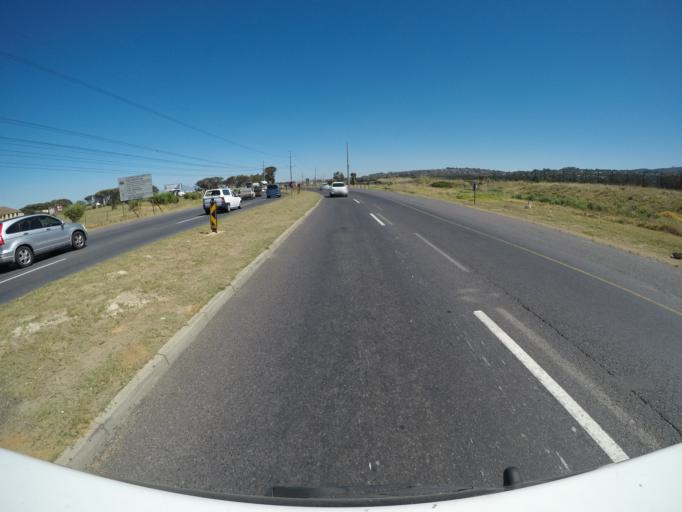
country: ZA
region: Western Cape
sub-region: Cape Winelands District Municipality
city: Stellenbosch
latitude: -34.0856
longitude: 18.8355
